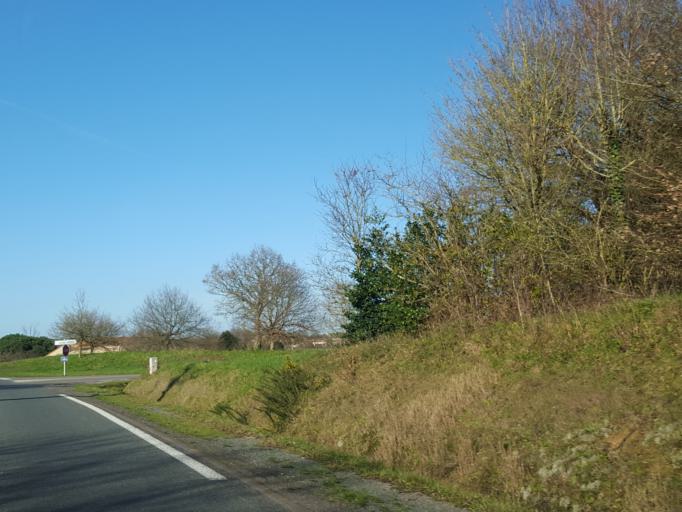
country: FR
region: Pays de la Loire
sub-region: Departement de la Vendee
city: La Roche-sur-Yon
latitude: 46.6679
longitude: -1.4675
